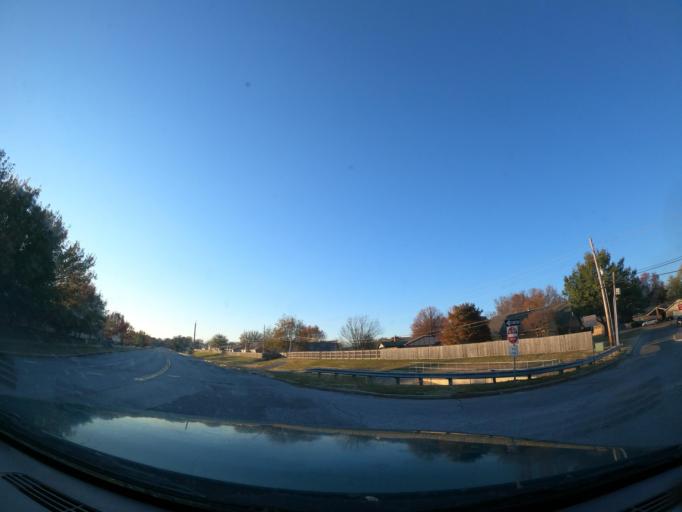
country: US
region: Oklahoma
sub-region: Tulsa County
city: Broken Arrow
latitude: 36.0678
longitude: -95.8819
